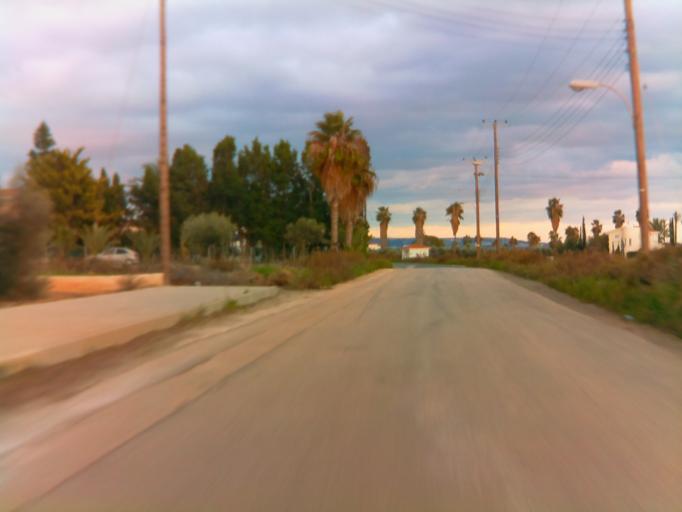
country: CY
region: Pafos
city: Pegeia
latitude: 34.8631
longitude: 32.3553
